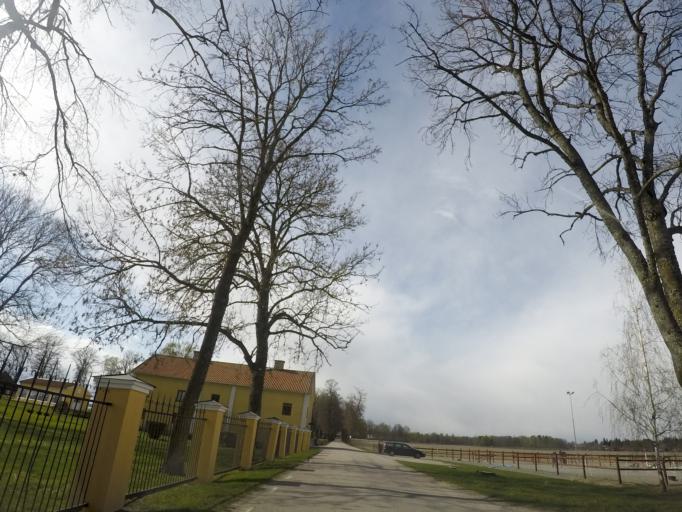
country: SE
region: Soedermanland
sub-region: Katrineholms Kommun
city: Katrineholm
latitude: 59.1380
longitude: 16.0603
